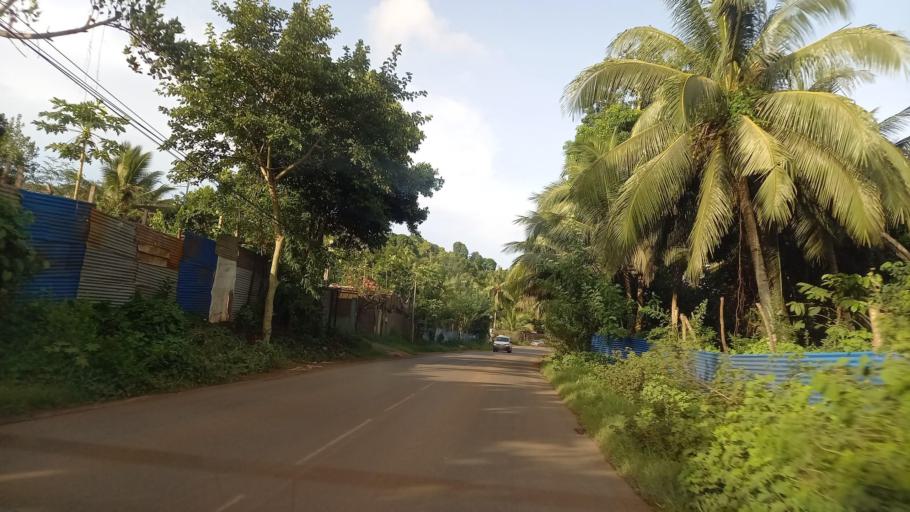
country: YT
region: Bandraboua
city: Bandraboua
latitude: -12.7280
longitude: 45.1204
